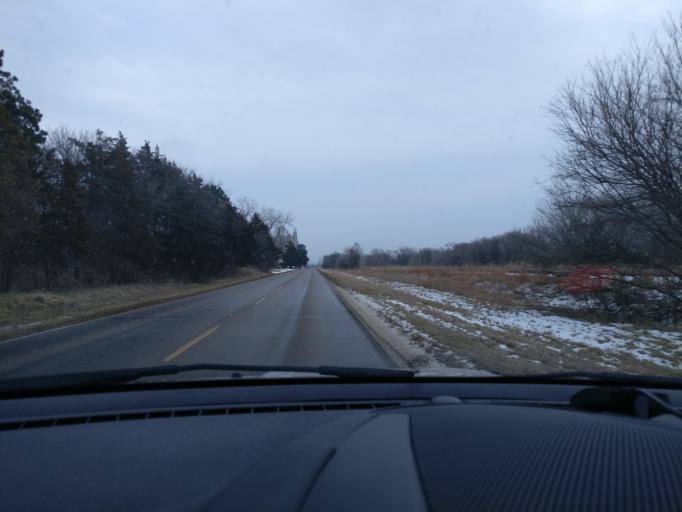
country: US
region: Nebraska
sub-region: Dodge County
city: Fremont
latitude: 41.4483
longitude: -96.5652
